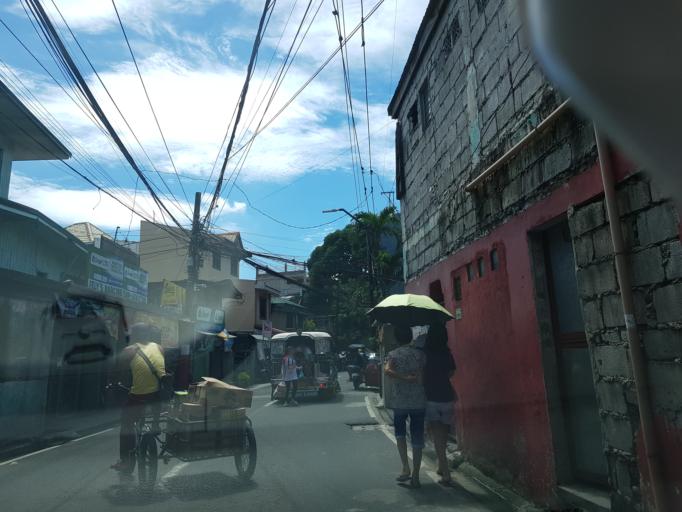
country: PH
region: Calabarzon
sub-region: Province of Rizal
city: Taguig
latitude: 14.5269
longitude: 121.0722
